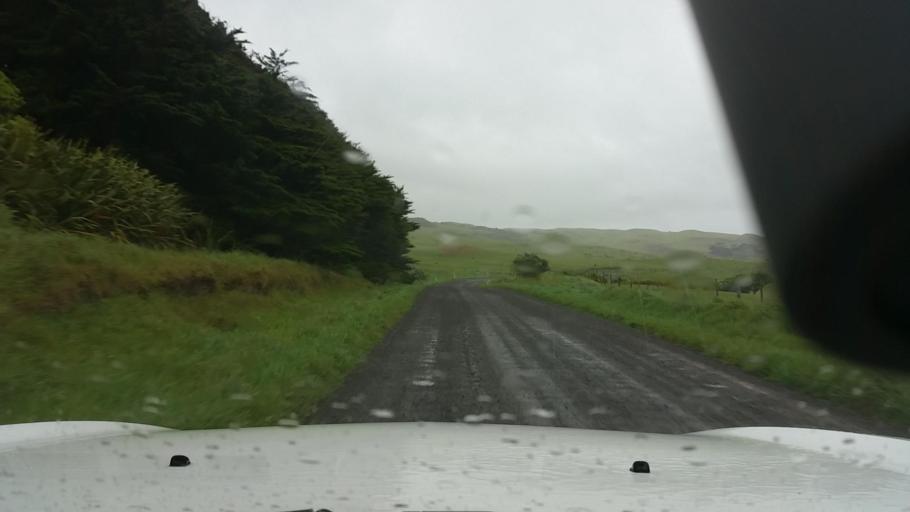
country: NZ
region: Chatham Islands
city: Waitangi
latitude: -43.9920
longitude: -176.6211
